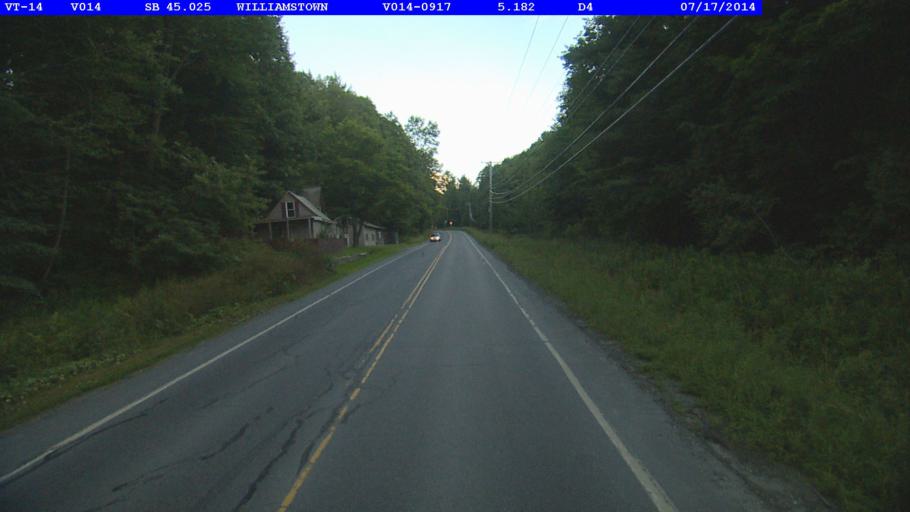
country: US
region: Vermont
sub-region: Orange County
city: Williamstown
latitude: 44.1310
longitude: -72.5357
